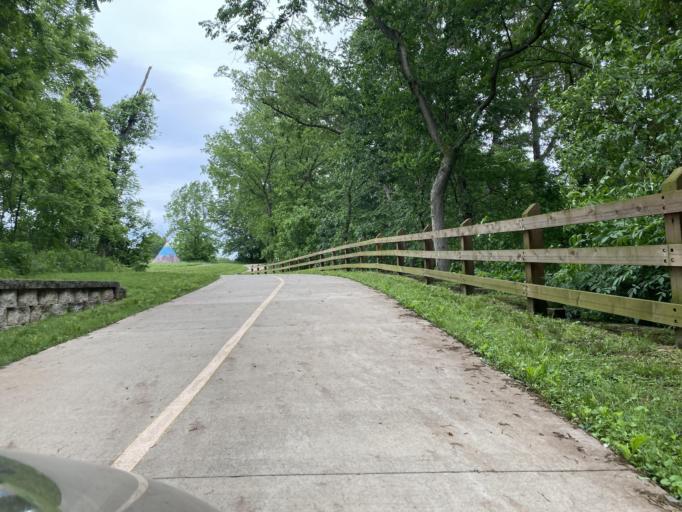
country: US
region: Arkansas
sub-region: Benton County
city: Bentonville
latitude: 36.3696
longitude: -94.2364
